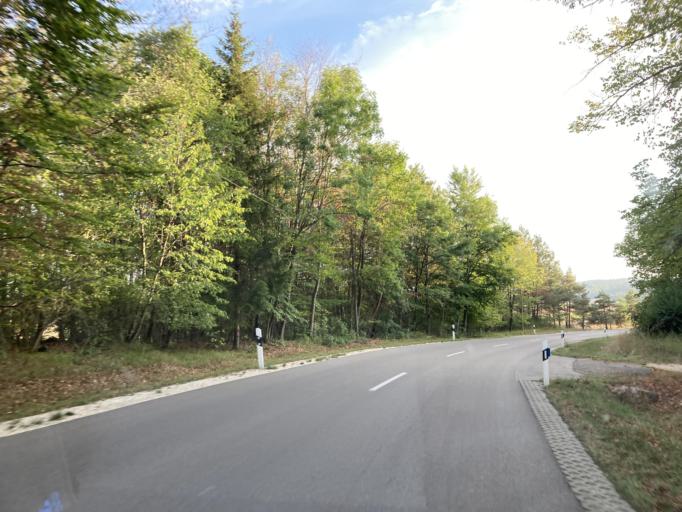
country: DE
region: Bavaria
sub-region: Swabia
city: Harburg
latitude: 48.7696
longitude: 10.6411
